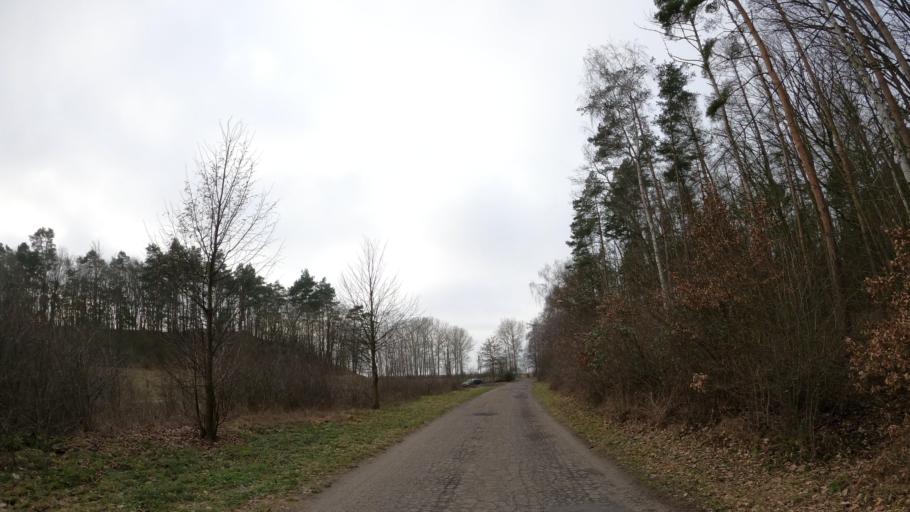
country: PL
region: West Pomeranian Voivodeship
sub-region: Powiat kamienski
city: Wolin
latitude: 53.8307
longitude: 14.6003
